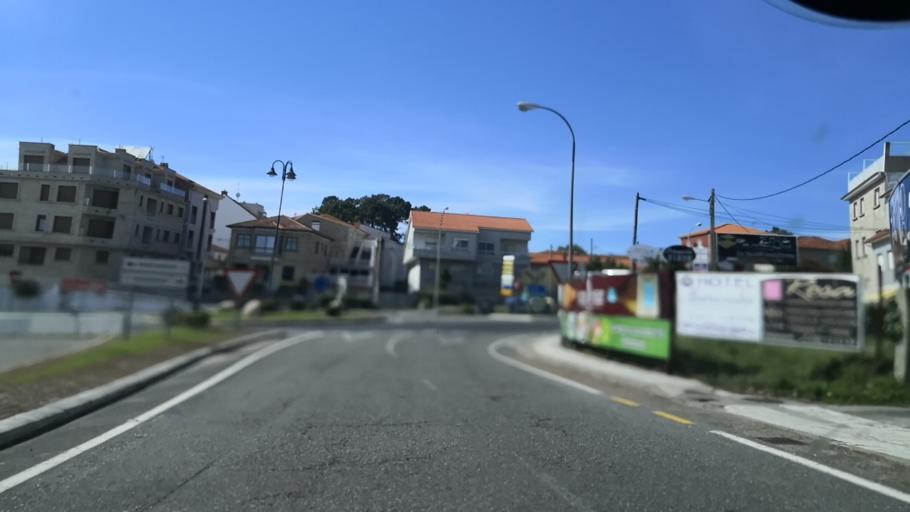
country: ES
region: Galicia
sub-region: Provincia de Pontevedra
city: Sanxenxo
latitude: 42.4002
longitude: -8.8192
